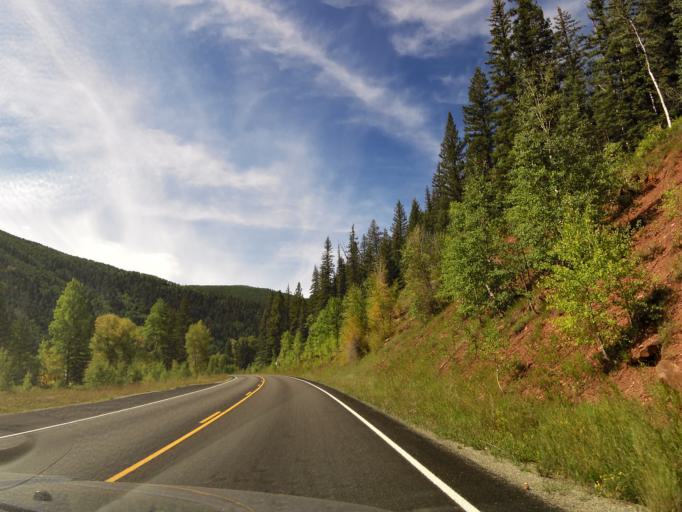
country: US
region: Colorado
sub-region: Montezuma County
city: Mancos
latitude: 37.5969
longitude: -108.1202
